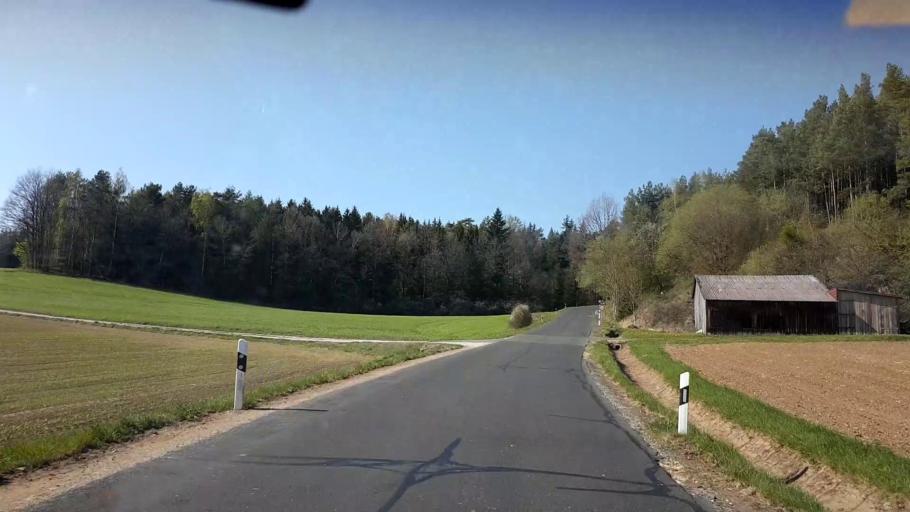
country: DE
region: Bavaria
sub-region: Upper Franconia
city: Waischenfeld
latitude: 49.8204
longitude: 11.3530
